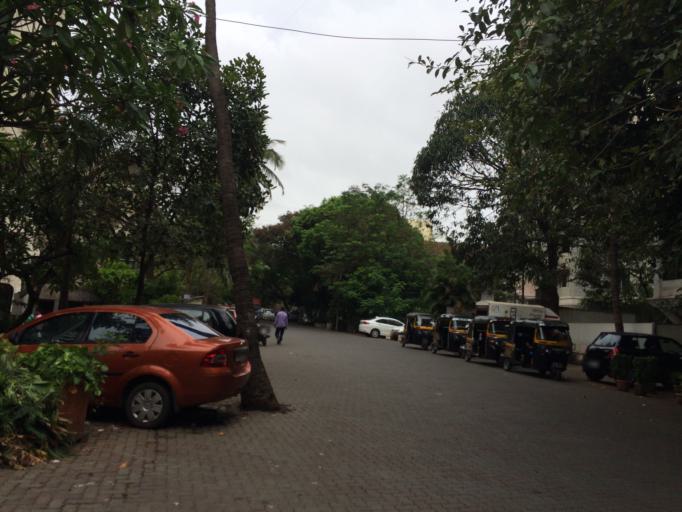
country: IN
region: Maharashtra
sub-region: Mumbai Suburban
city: Mumbai
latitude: 19.0487
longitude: 72.8224
